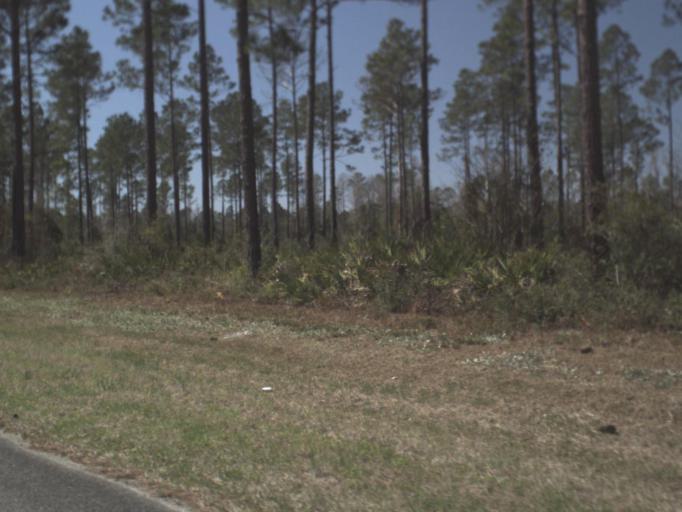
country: US
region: Florida
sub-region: Leon County
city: Woodville
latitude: 30.3318
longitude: -84.0269
